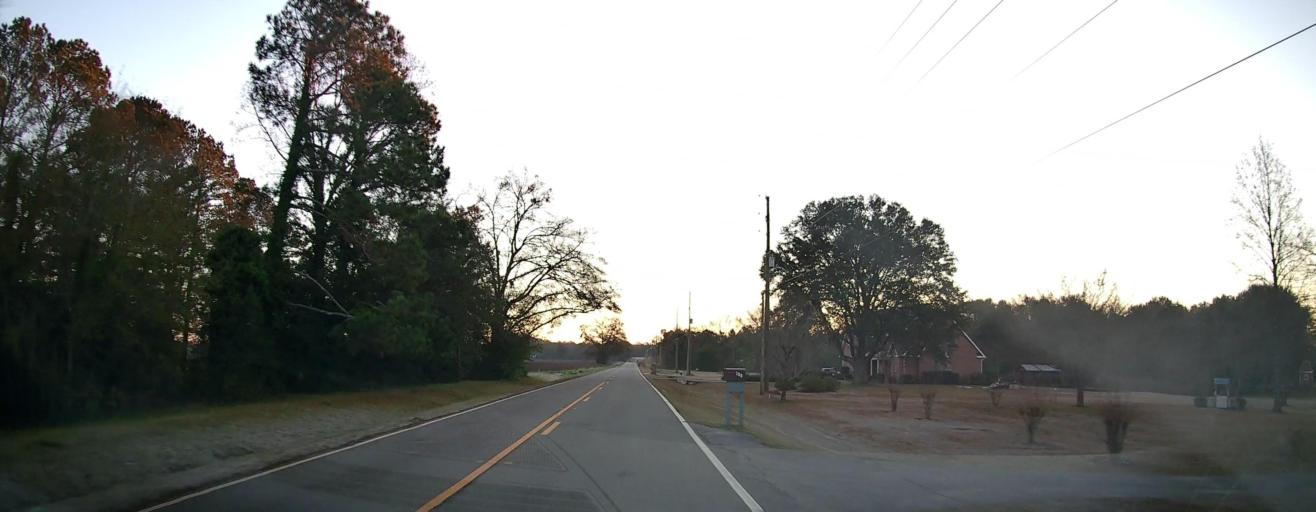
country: US
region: Georgia
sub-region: Houston County
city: Centerville
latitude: 32.6430
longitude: -83.7072
